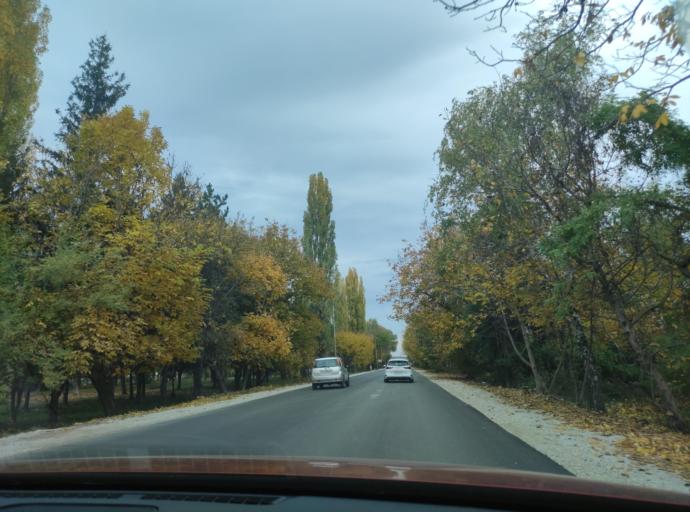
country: BG
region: Montana
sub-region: Obshtina Montana
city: Montana
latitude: 43.3983
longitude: 23.2403
